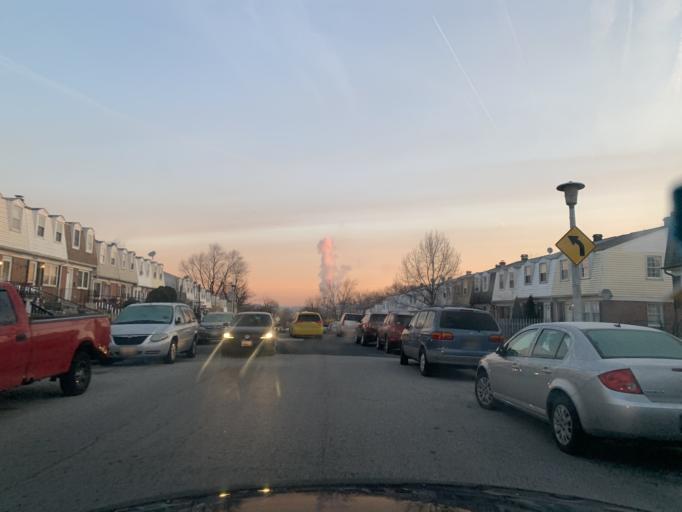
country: US
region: Maryland
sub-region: Baltimore County
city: Baltimore Highlands
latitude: 39.2521
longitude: -76.6417
